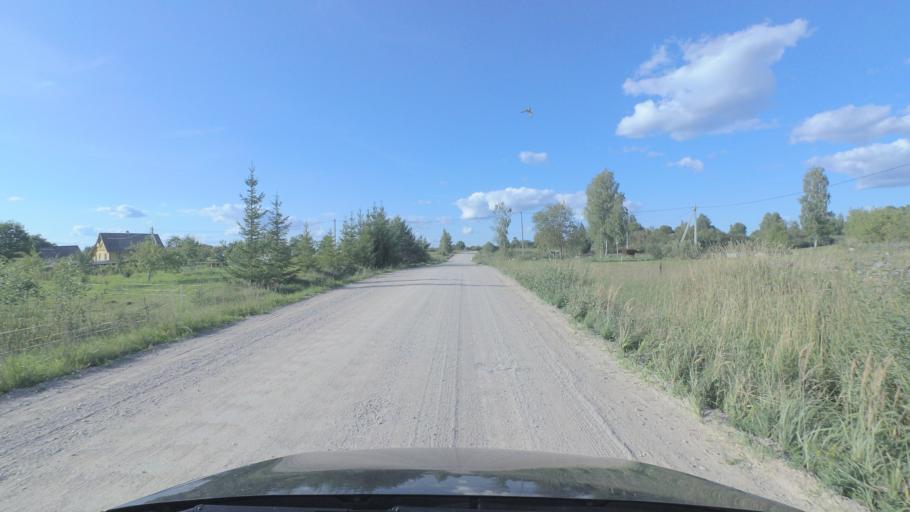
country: LT
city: Pabrade
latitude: 55.1266
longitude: 25.7052
